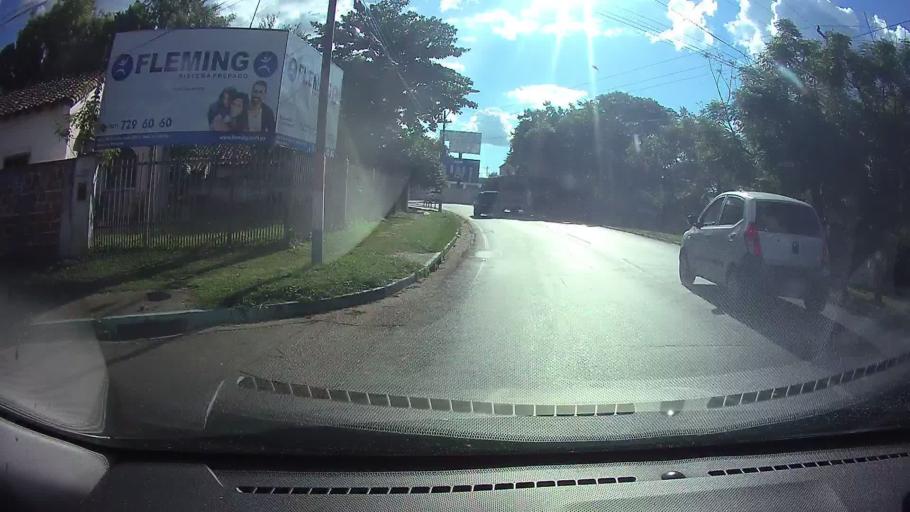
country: PY
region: Cordillera
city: Caacupe
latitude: -25.3825
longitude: -57.1366
